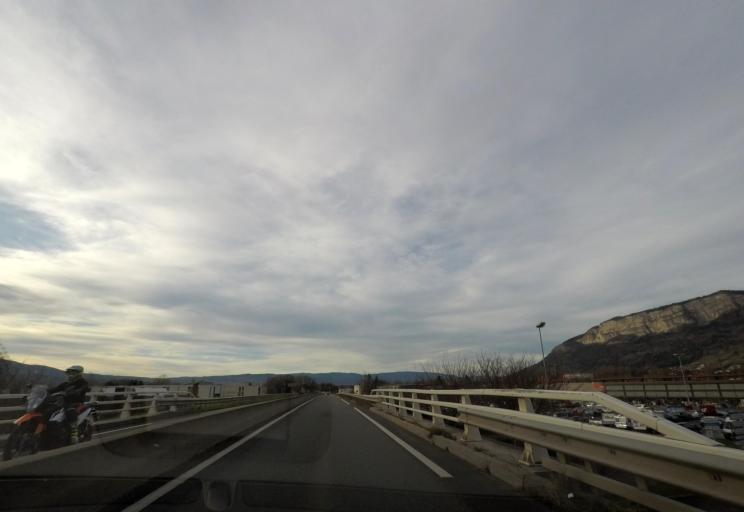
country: FR
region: Rhone-Alpes
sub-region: Departement de la Haute-Savoie
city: Bonneville
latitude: 46.0720
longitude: 6.4206
